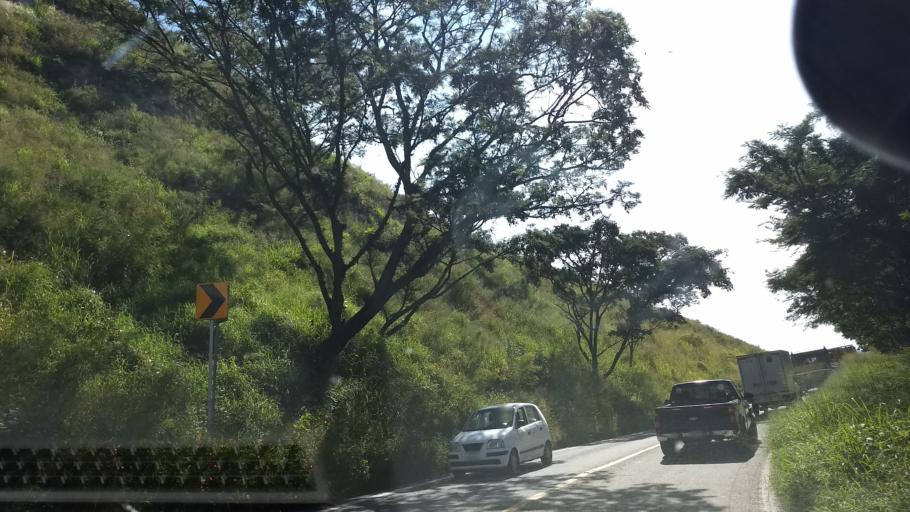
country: MX
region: Jalisco
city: Tuxpan
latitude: 19.5255
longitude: -103.4244
